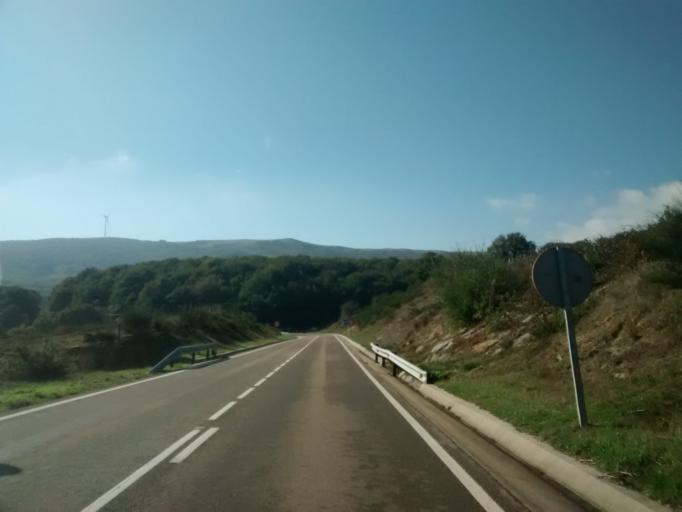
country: ES
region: Cantabria
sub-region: Provincia de Cantabria
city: Reinosa
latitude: 42.9812
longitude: -4.1041
